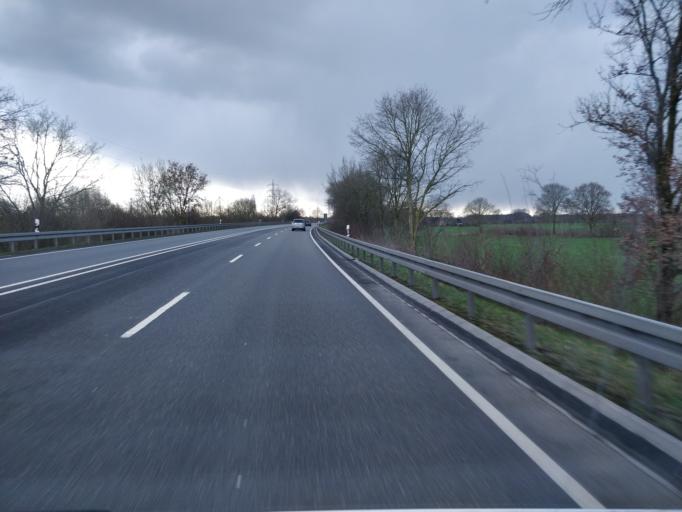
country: DE
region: North Rhine-Westphalia
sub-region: Regierungsbezirk Dusseldorf
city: Bocholt
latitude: 51.8109
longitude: 6.5927
